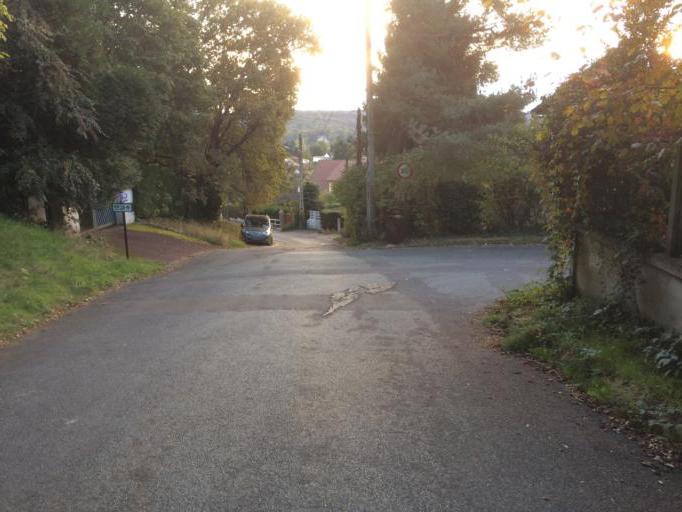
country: FR
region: Ile-de-France
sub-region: Departement des Yvelines
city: Saint-Remy-les-Chevreuse
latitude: 48.7108
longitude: 2.0712
